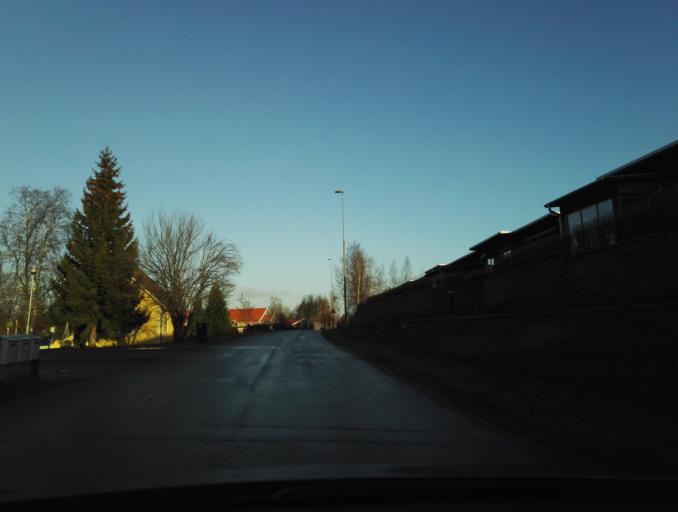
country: SE
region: Kronoberg
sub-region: Vaxjo Kommun
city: Vaexjoe
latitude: 56.9048
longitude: 14.7992
